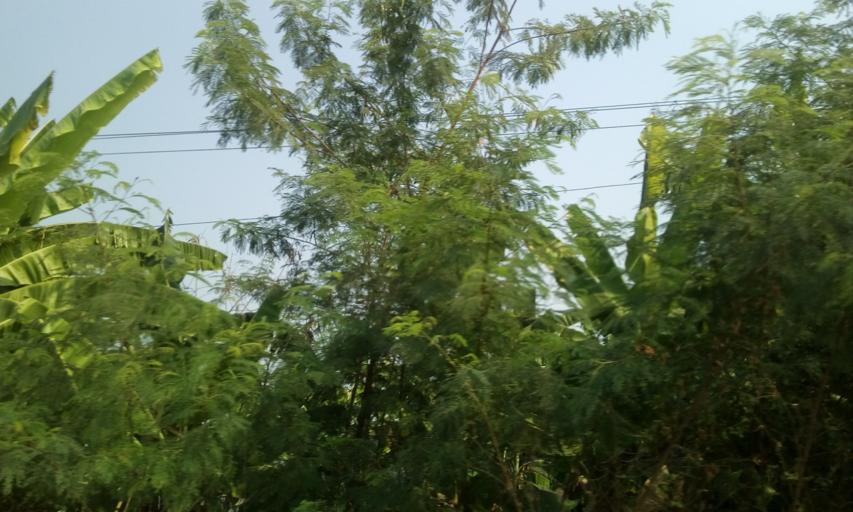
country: TH
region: Pathum Thani
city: Ban Lam Luk Ka
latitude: 13.9929
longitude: 100.7564
